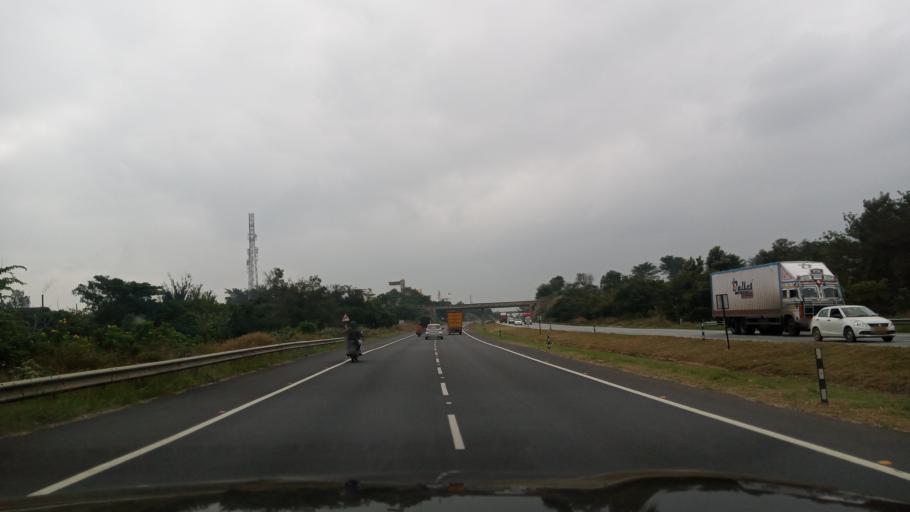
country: IN
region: Karnataka
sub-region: Bangalore Rural
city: Nelamangala
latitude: 13.0157
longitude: 77.4762
